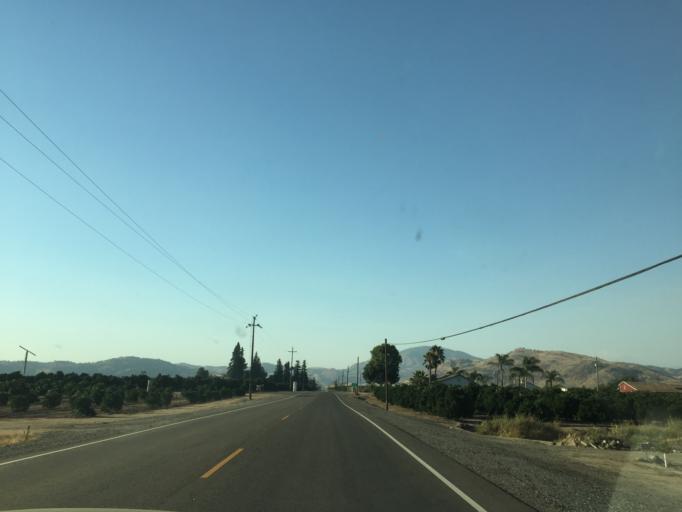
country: US
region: California
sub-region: Fresno County
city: Orange Cove
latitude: 36.6435
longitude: -119.3047
